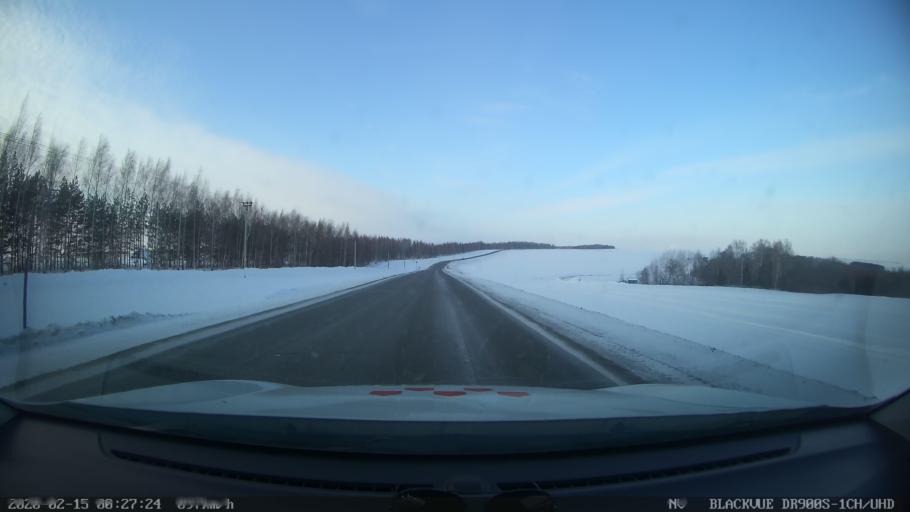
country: RU
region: Tatarstan
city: Verkhniy Uslon
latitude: 55.6276
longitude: 48.8747
